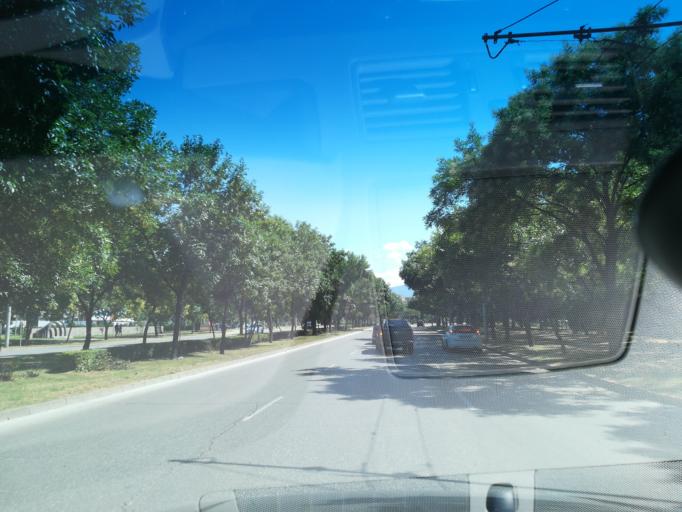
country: BG
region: Plovdiv
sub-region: Obshtina Plovdiv
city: Plovdiv
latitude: 42.1377
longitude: 24.7913
